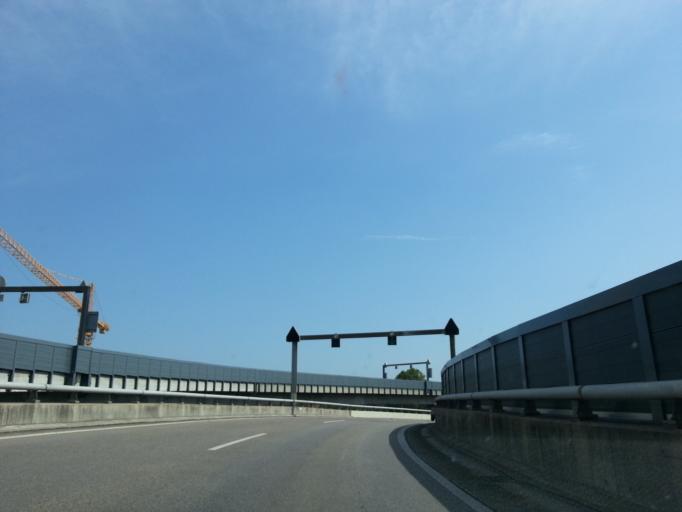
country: DE
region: Baden-Wuerttemberg
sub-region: Freiburg Region
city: Weil am Rhein
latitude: 47.5737
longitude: 7.5988
